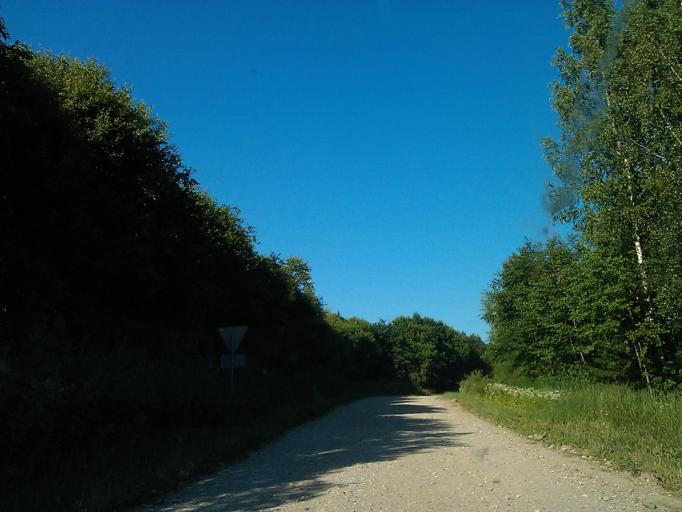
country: LV
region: Raunas
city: Rauna
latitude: 57.2556
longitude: 25.5444
